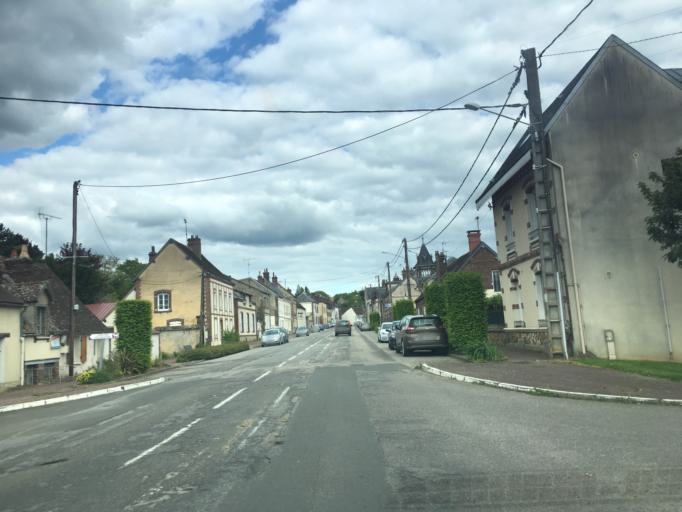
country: FR
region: Haute-Normandie
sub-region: Departement de l'Eure
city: Nonancourt
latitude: 48.7733
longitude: 1.1926
